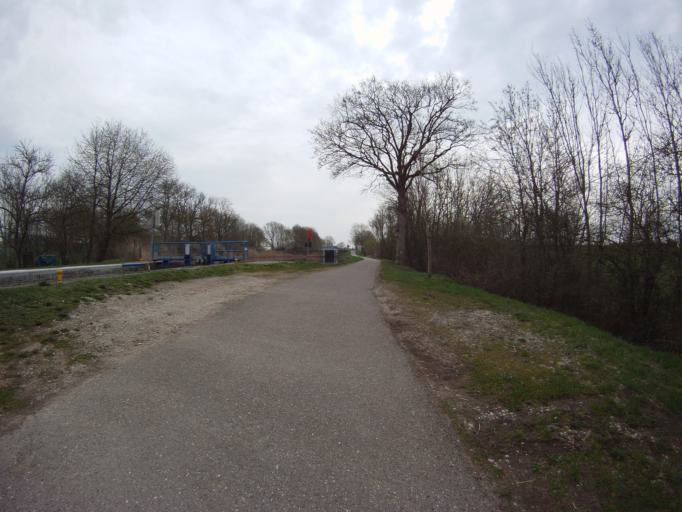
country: FR
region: Lorraine
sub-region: Departement de Meurthe-et-Moselle
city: Fleville-devant-Nancy
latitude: 48.6297
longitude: 6.2159
